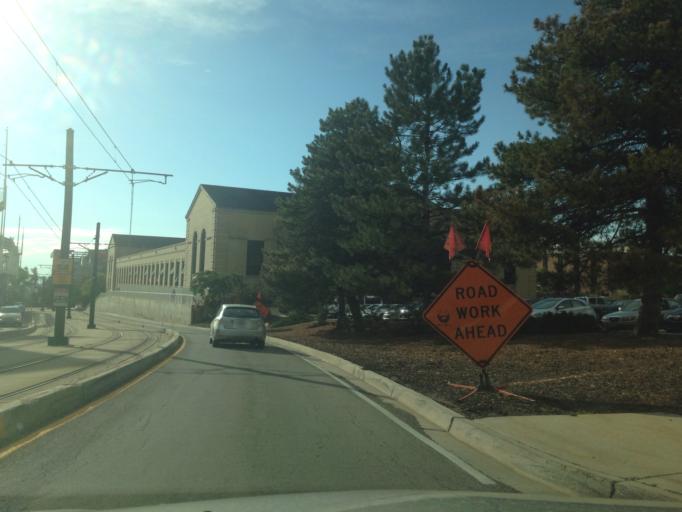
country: US
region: Utah
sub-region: Salt Lake County
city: Salt Lake City
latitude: 40.7609
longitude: -111.8476
